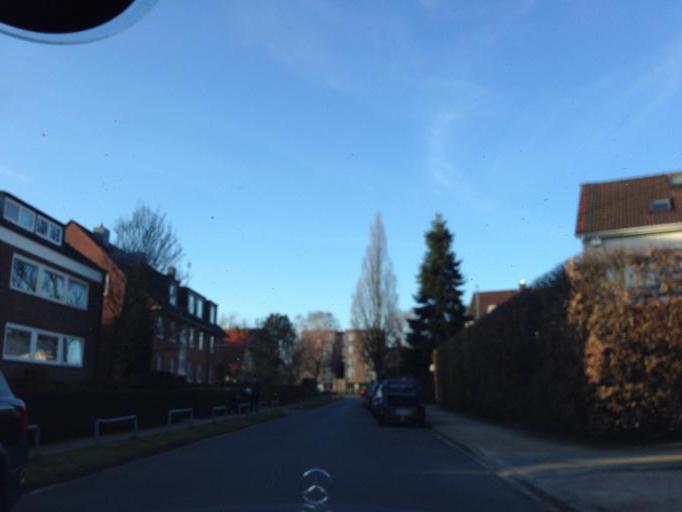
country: DE
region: Hamburg
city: Farmsen-Berne
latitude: 53.5988
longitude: 10.1335
